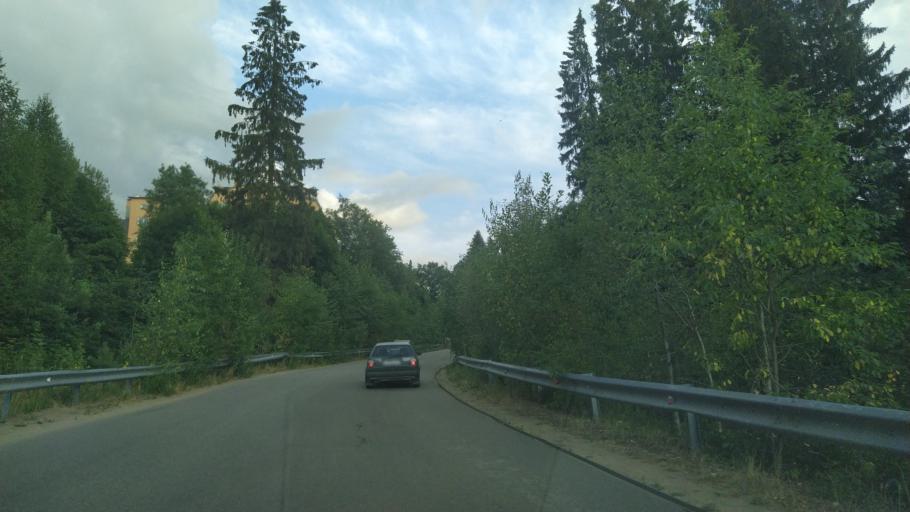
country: RU
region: Leningrad
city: Toksovo
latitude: 60.1671
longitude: 30.5369
